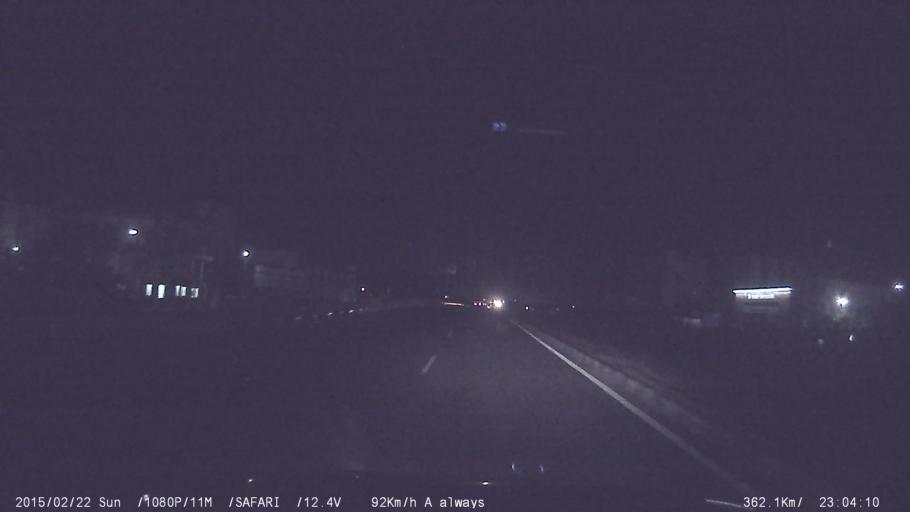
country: IN
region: Tamil Nadu
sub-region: Namakkal
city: Rasipuram
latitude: 11.3988
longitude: 78.1601
